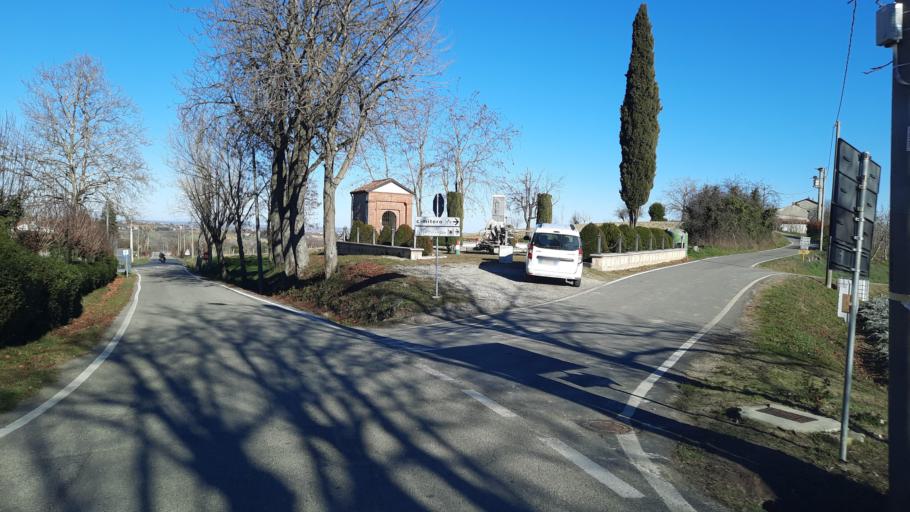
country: IT
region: Piedmont
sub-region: Provincia di Alessandria
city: Olivola
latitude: 45.0368
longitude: 8.3713
